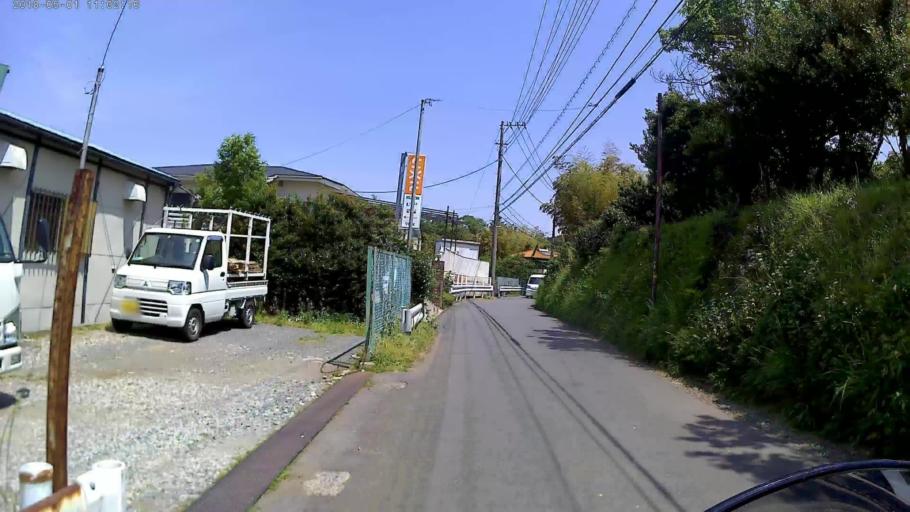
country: JP
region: Kanagawa
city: Minami-rinkan
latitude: 35.4814
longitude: 139.5192
